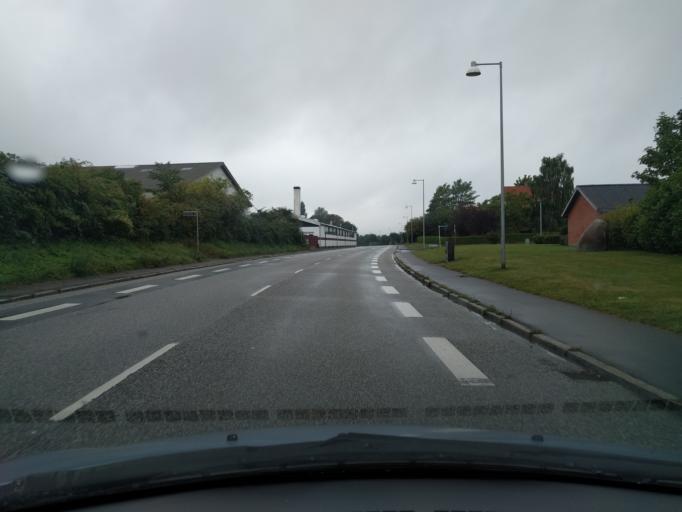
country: DK
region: Zealand
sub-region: Guldborgsund Kommune
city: Stubbekobing
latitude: 54.8883
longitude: 12.0316
